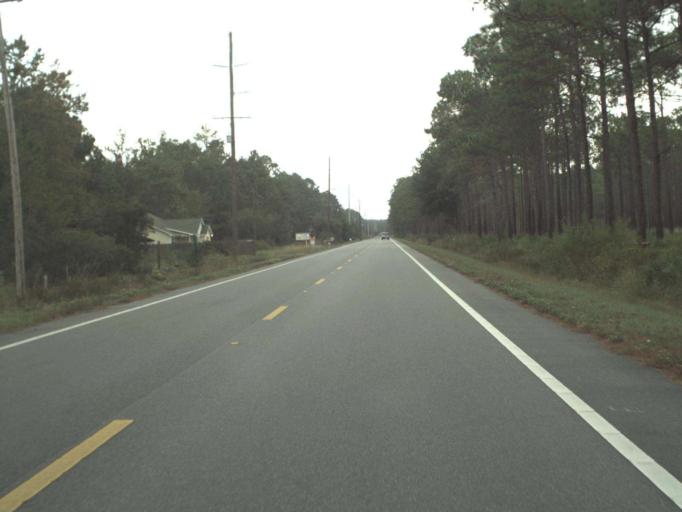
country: US
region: Florida
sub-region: Wakulla County
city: Crawfordville
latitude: 30.0385
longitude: -84.4961
